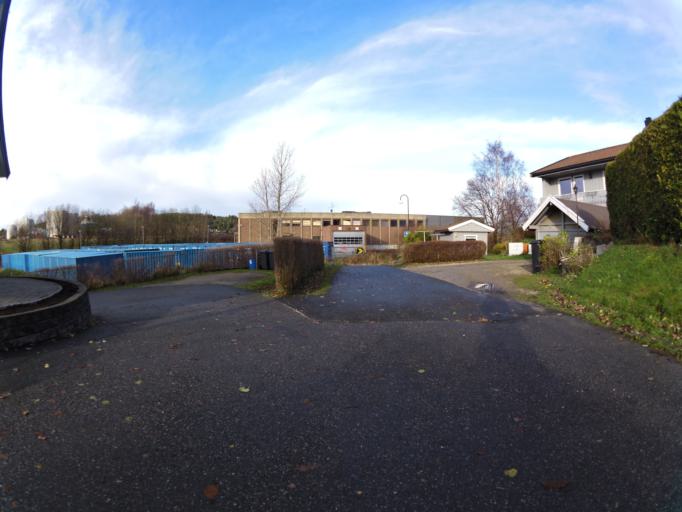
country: NO
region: Ostfold
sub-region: Sarpsborg
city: Sarpsborg
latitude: 59.2708
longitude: 11.0805
